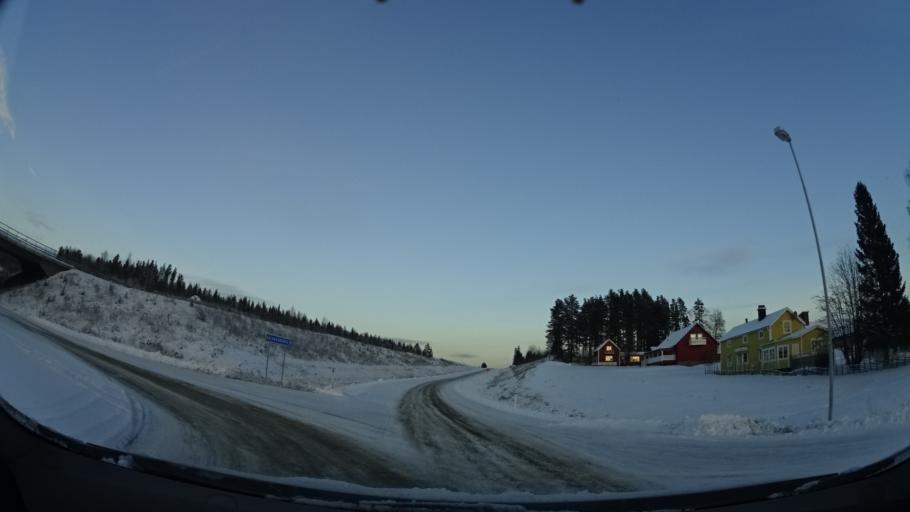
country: SE
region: Vaesterbotten
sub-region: Skelleftea Kommun
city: Kage
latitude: 64.8677
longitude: 21.0217
